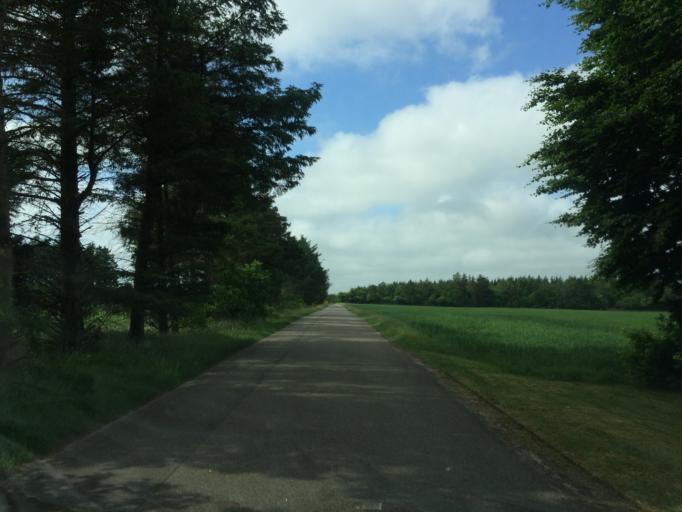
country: DK
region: Central Jutland
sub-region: Holstebro Kommune
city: Ulfborg
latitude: 56.2293
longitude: 8.4363
